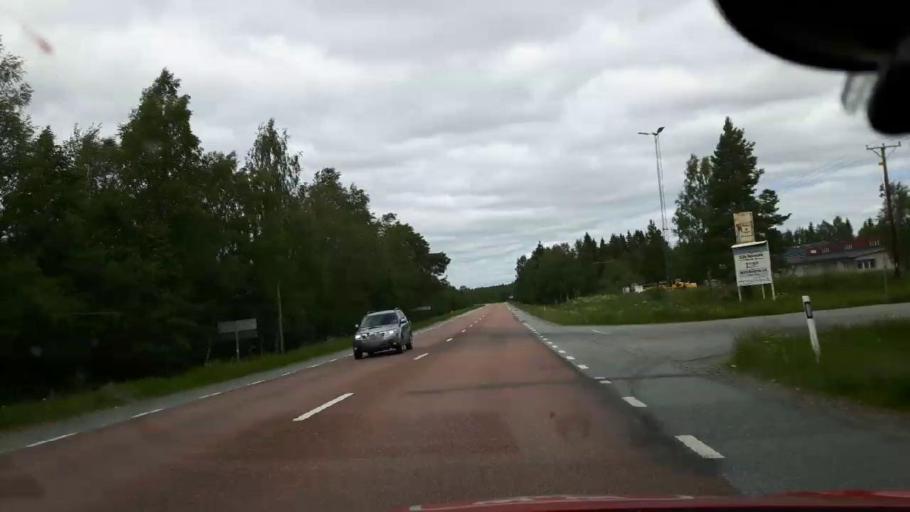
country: SE
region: Jaemtland
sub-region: Braecke Kommun
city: Braecke
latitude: 62.9082
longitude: 15.2635
